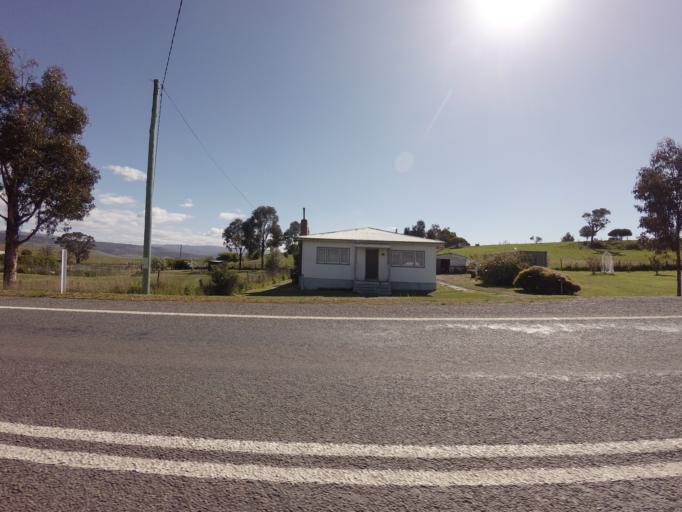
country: AU
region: Tasmania
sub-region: Derwent Valley
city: New Norfolk
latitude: -42.7012
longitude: 146.9419
